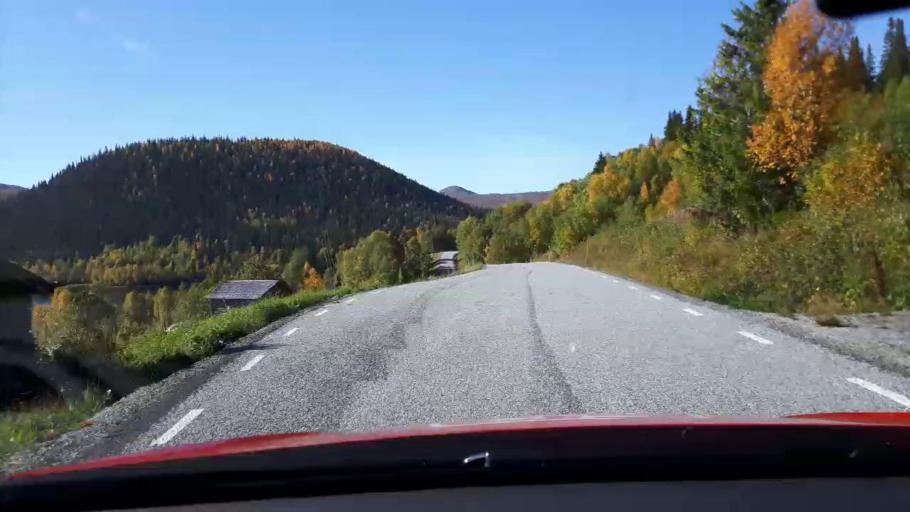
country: NO
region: Nord-Trondelag
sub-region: Royrvik
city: Royrvik
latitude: 64.8773
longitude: 14.2265
